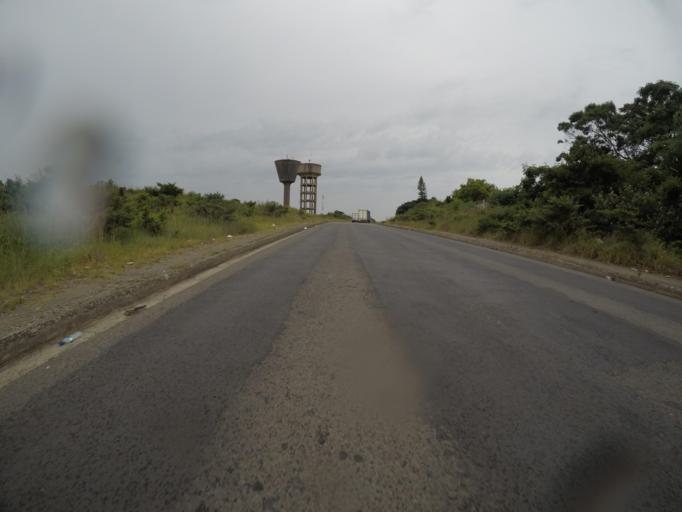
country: ZA
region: Eastern Cape
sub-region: Buffalo City Metropolitan Municipality
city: East London
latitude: -32.9684
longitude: 27.8278
